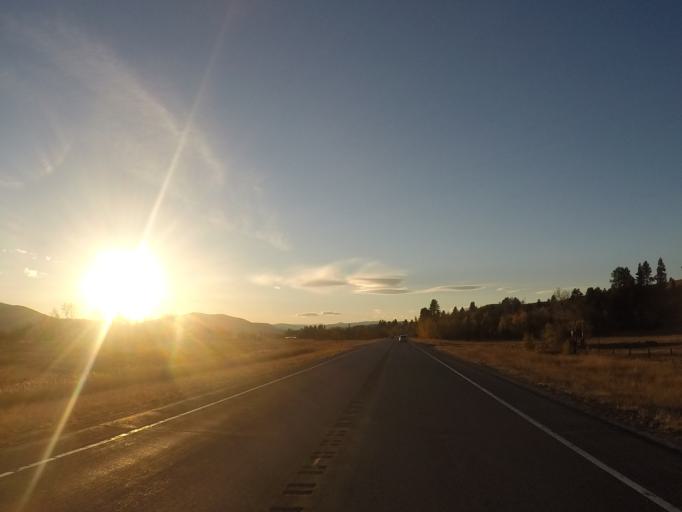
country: US
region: Montana
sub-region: Lewis and Clark County
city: Lincoln
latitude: 47.0165
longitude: -113.0757
